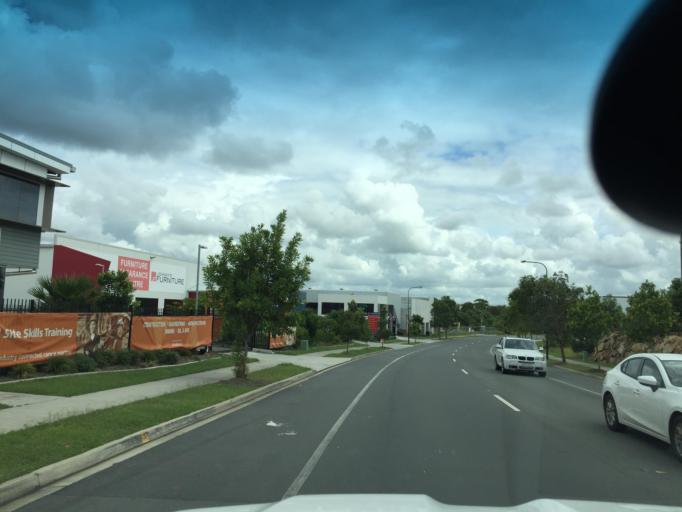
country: AU
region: Queensland
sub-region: Moreton Bay
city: Mango Hill
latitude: -27.2181
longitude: 152.9977
